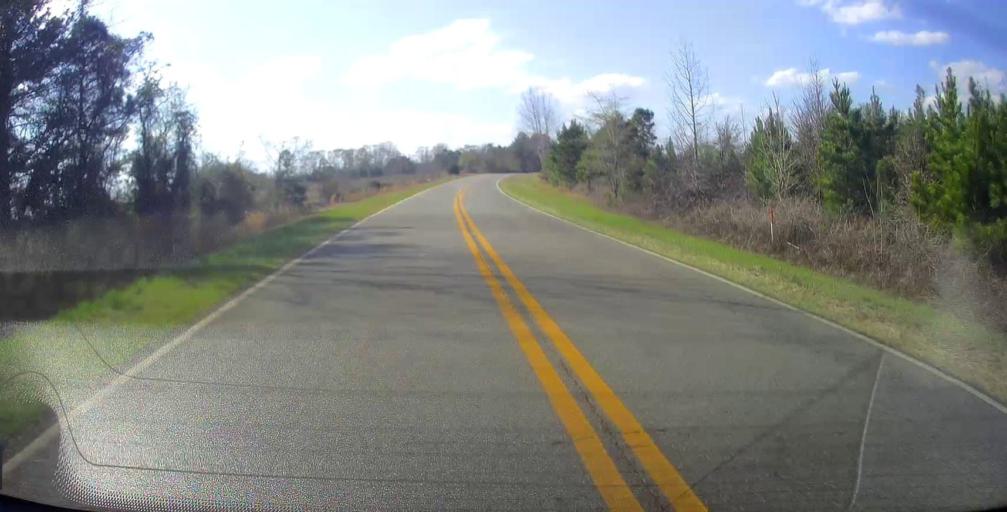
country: US
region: Georgia
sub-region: Laurens County
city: Dublin
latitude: 32.5696
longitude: -83.0394
